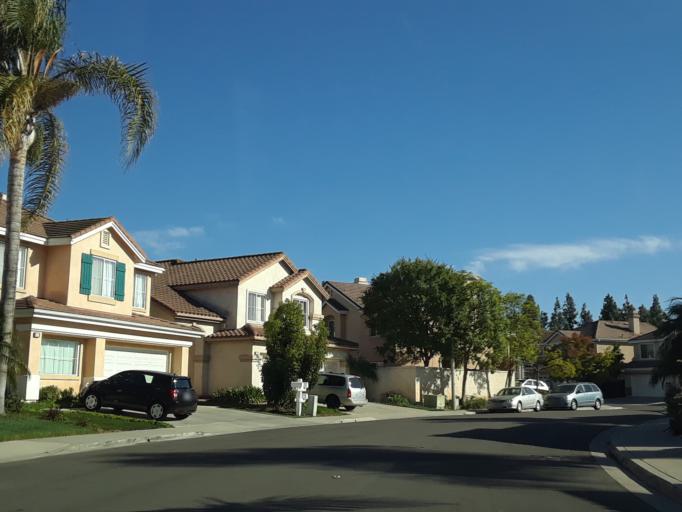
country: US
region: California
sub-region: Orange County
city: Irvine
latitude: 33.6936
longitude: -117.8011
